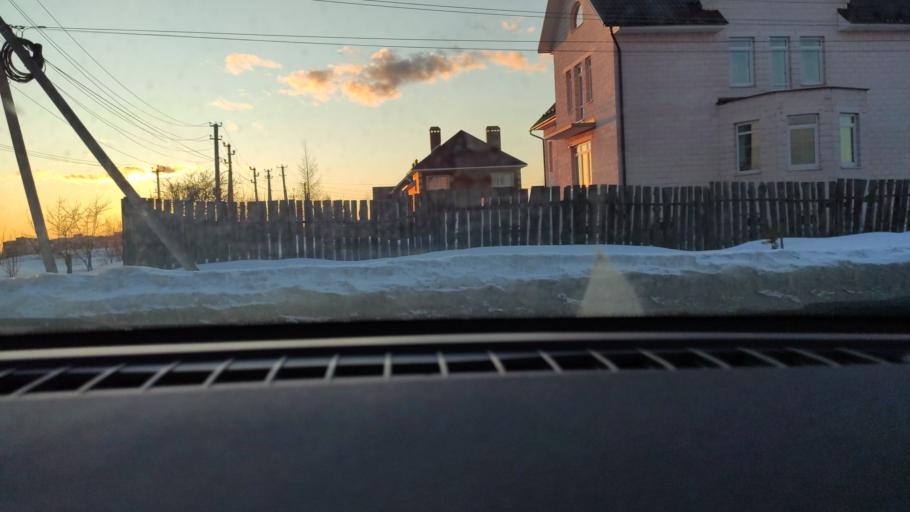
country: RU
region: Perm
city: Perm
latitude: 58.0366
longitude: 56.3715
